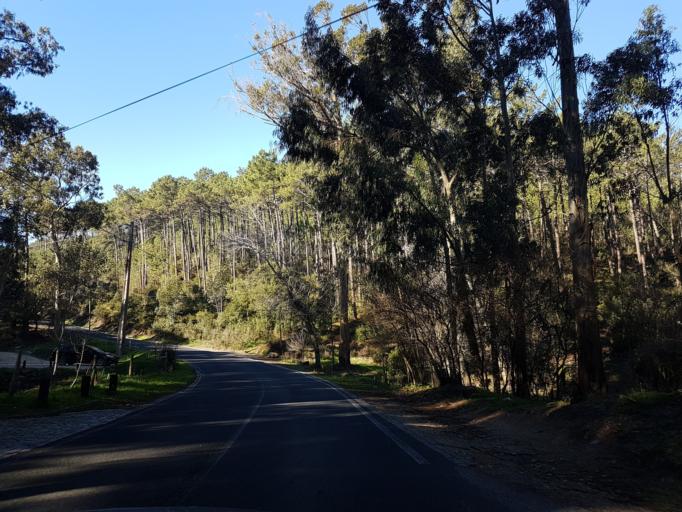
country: PT
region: Lisbon
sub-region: Cascais
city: Alcabideche
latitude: 38.7588
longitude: -9.4192
